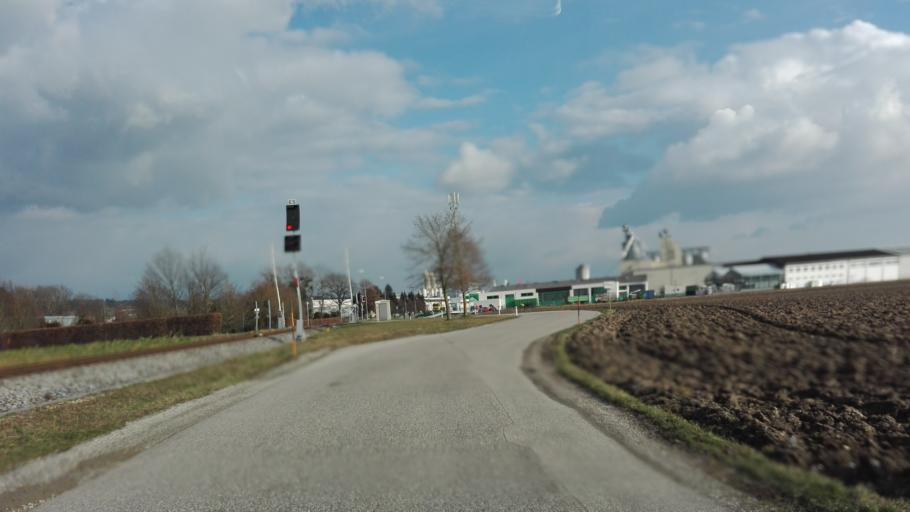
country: AT
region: Upper Austria
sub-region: Politischer Bezirk Perg
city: Perg
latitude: 48.2489
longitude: 14.6202
